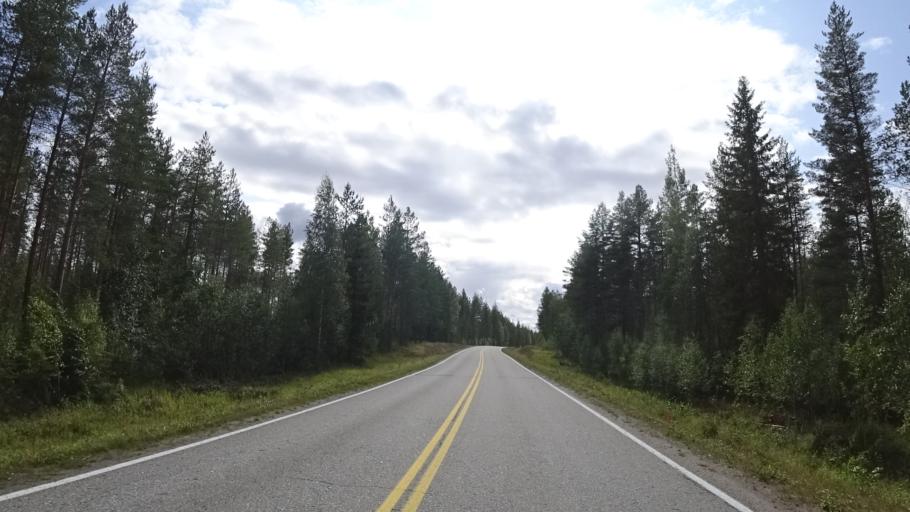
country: FI
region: North Karelia
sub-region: Joensuu
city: Ilomantsi
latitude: 62.7913
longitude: 31.0989
